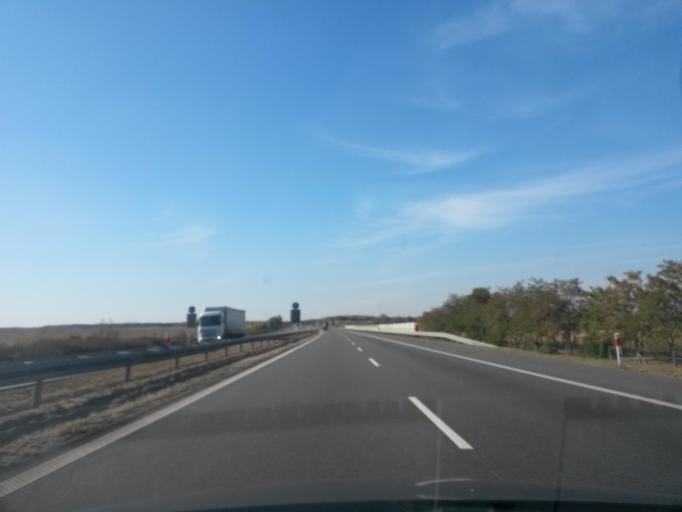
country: PL
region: Opole Voivodeship
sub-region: Powiat opolski
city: Proszkow
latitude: 50.5738
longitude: 17.8520
